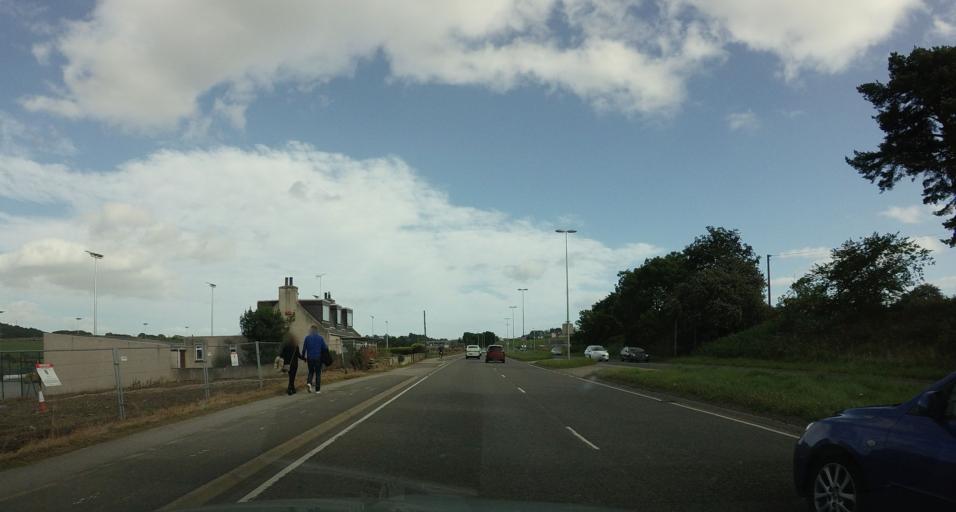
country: GB
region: Scotland
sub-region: Aberdeenshire
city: Westhill
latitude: 57.1473
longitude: -2.2581
